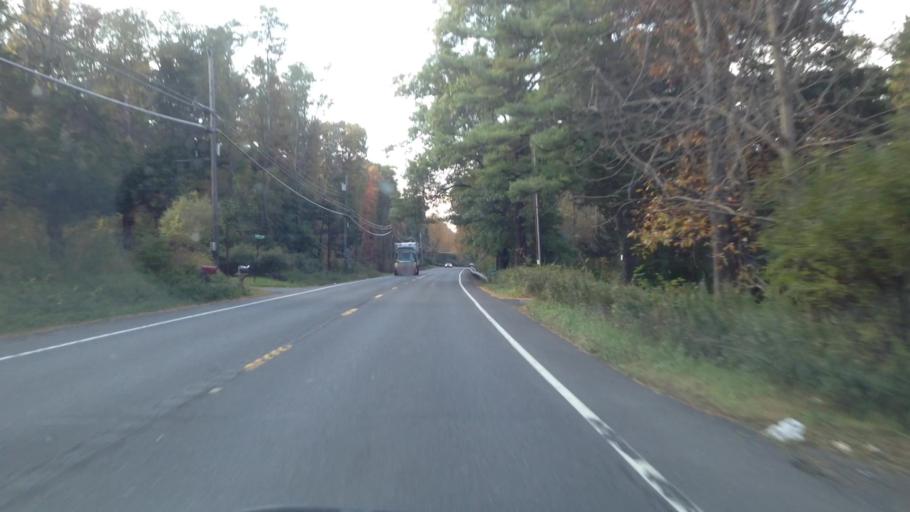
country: US
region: New York
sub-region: Ulster County
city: Tillson
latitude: 41.7867
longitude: -74.0700
